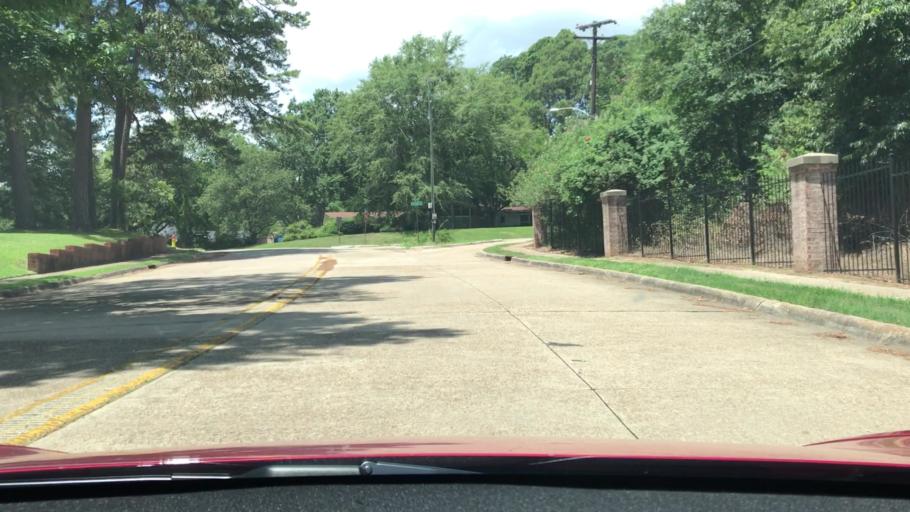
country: US
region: Louisiana
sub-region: Bossier Parish
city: Bossier City
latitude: 32.4358
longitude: -93.7317
